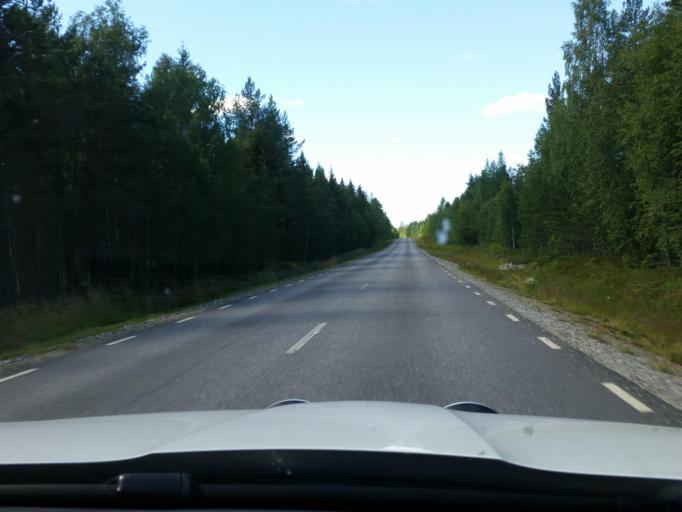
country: SE
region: Norrbotten
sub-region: Pitea Kommun
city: Roknas
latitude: 65.1965
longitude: 21.1129
